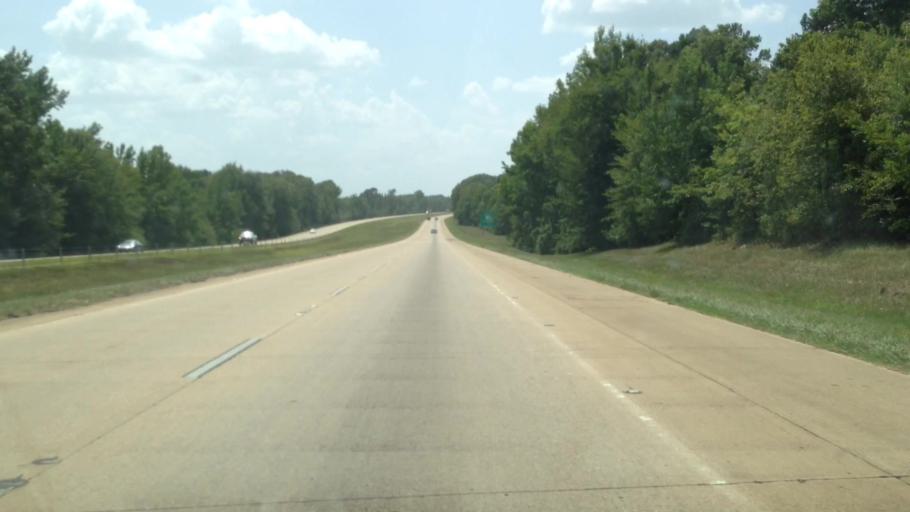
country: US
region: Louisiana
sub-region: Lincoln Parish
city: Grambling
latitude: 32.5407
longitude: -92.6931
